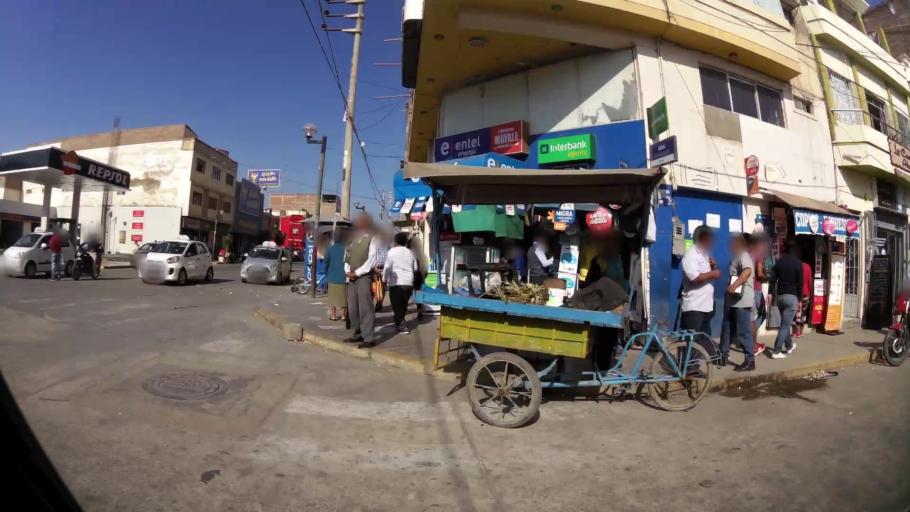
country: PE
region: Lambayeque
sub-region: Provincia de Chiclayo
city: Chiclayo
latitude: -6.7679
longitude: -79.8419
